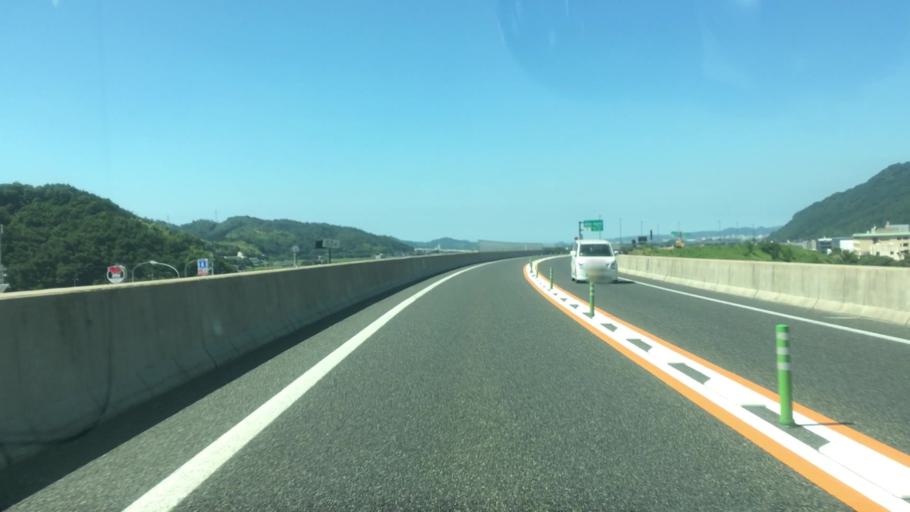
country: JP
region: Tottori
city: Tottori
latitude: 35.4186
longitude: 134.2056
